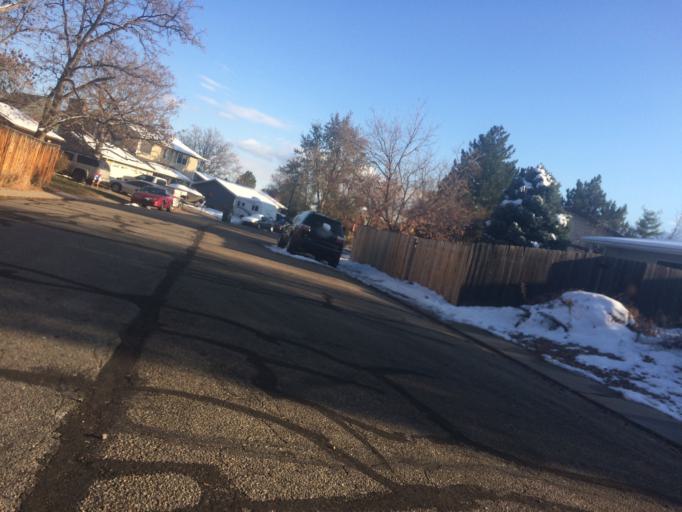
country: US
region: Colorado
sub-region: Boulder County
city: Lafayette
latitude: 39.9886
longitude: -105.1056
